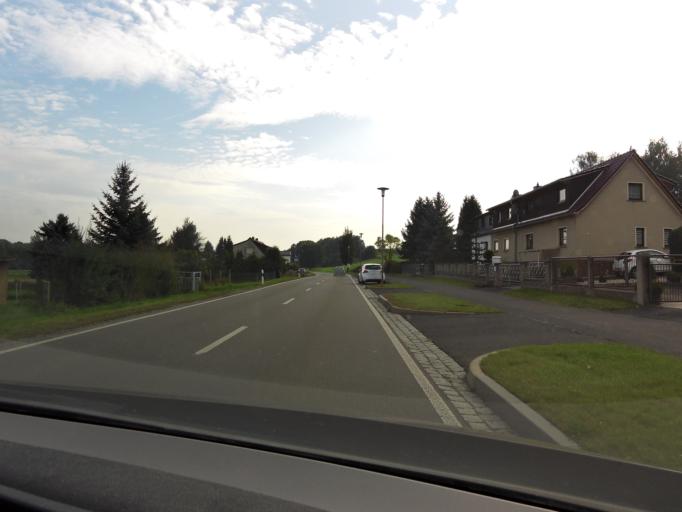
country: DE
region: Thuringia
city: Fambach
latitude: 50.7527
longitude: 10.3612
